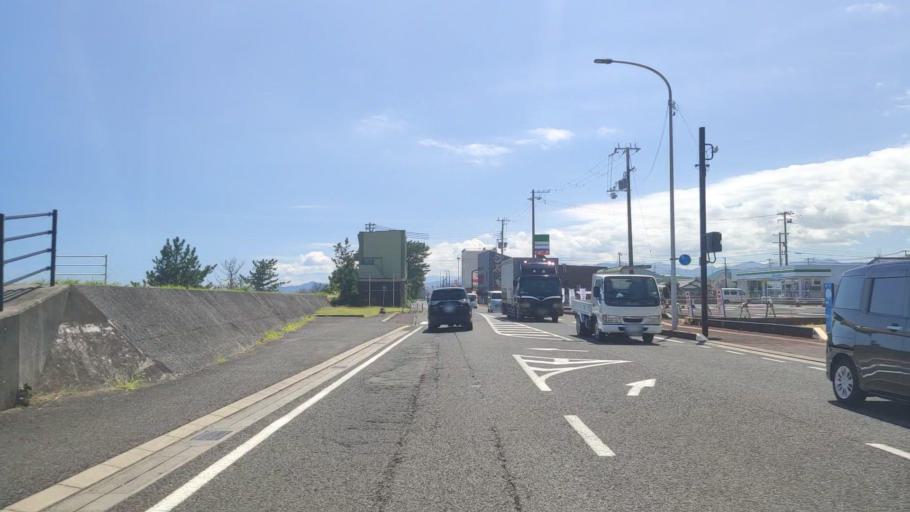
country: JP
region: Wakayama
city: Shingu
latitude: 33.8783
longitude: 136.0921
